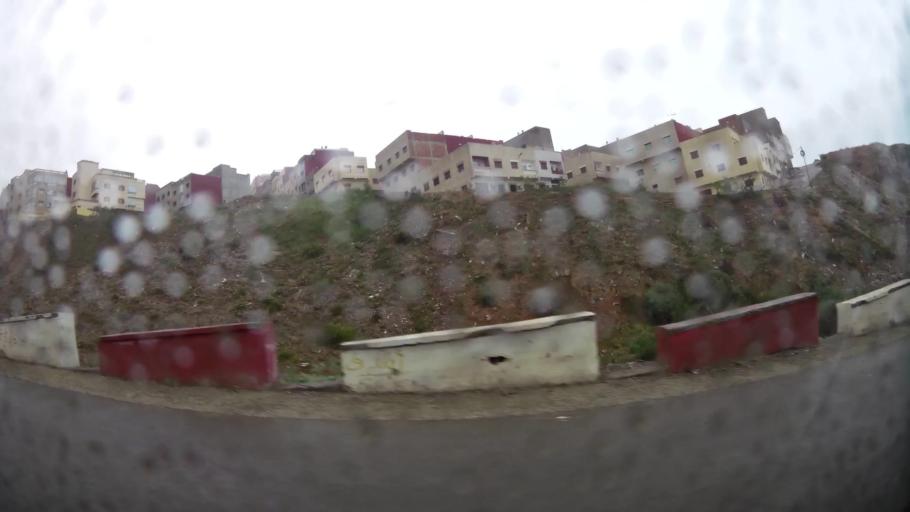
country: MA
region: Taza-Al Hoceima-Taounate
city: Al Hoceima
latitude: 35.2575
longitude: -3.9375
